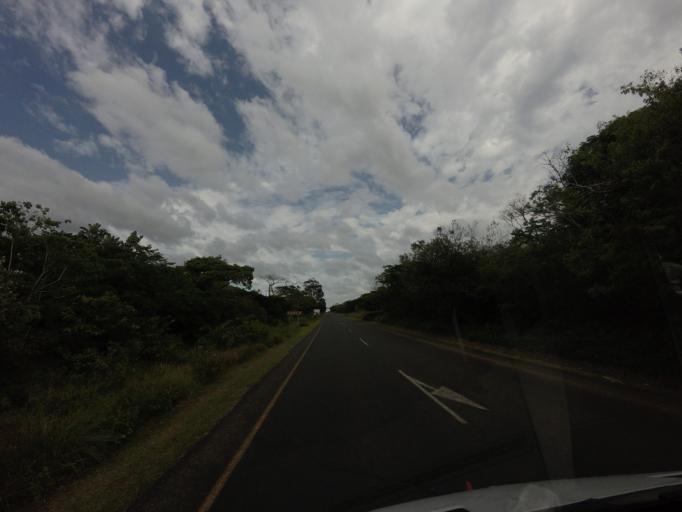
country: ZA
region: KwaZulu-Natal
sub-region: uMkhanyakude District Municipality
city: Mtubatuba
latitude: -28.3739
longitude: 32.3936
